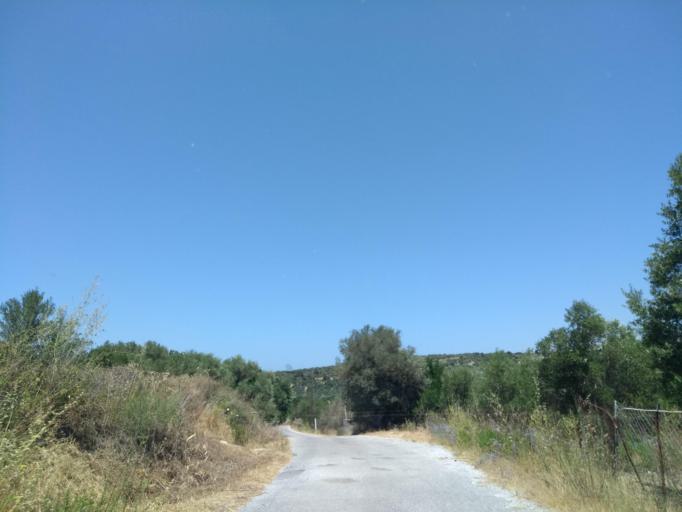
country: GR
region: Crete
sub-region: Nomos Chanias
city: Georgioupolis
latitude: 35.3277
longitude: 24.3185
